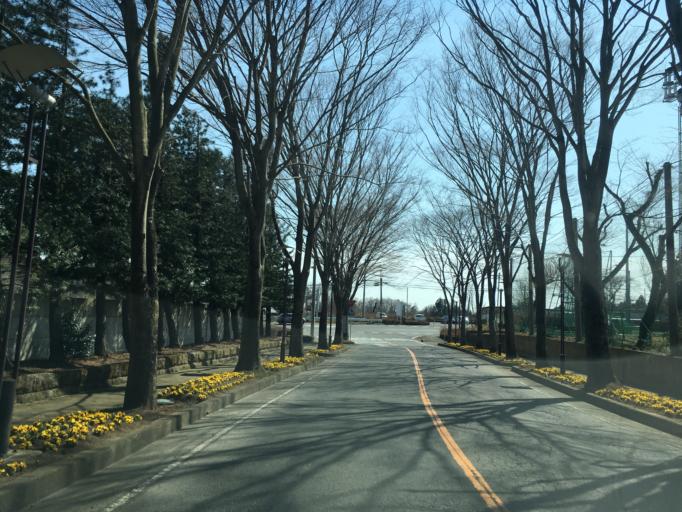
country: JP
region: Tochigi
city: Kuroiso
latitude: 37.0464
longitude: 140.0249
